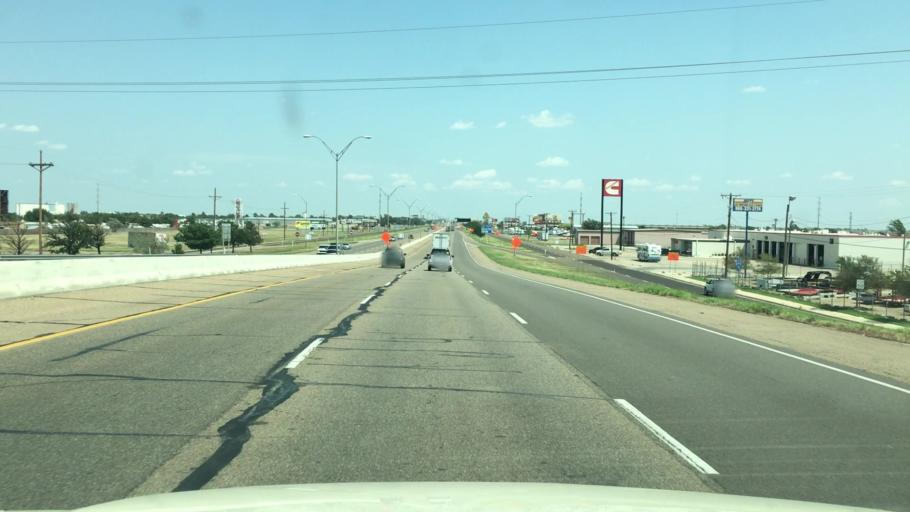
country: US
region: Texas
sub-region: Potter County
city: Amarillo
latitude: 35.1926
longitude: -101.7778
